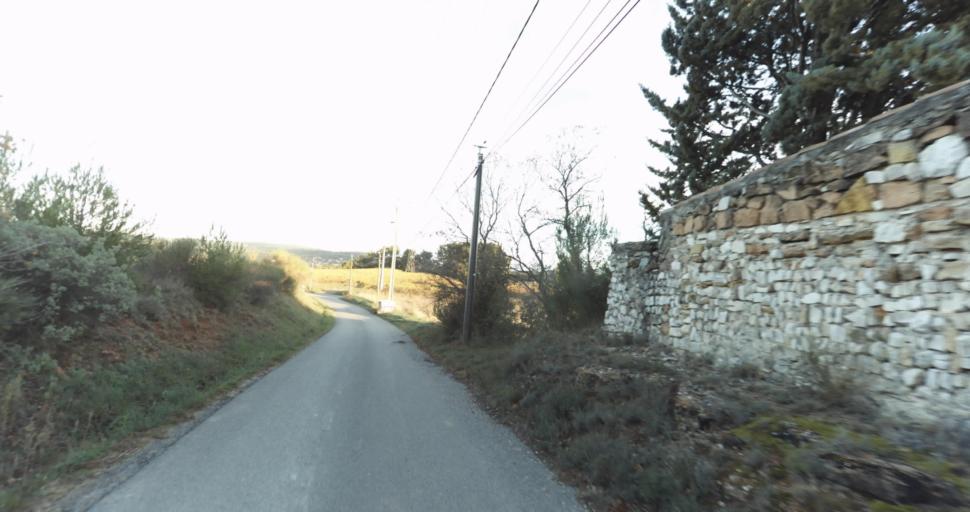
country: FR
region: Provence-Alpes-Cote d'Azur
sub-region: Departement des Bouches-du-Rhone
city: Venelles
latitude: 43.5756
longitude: 5.4930
